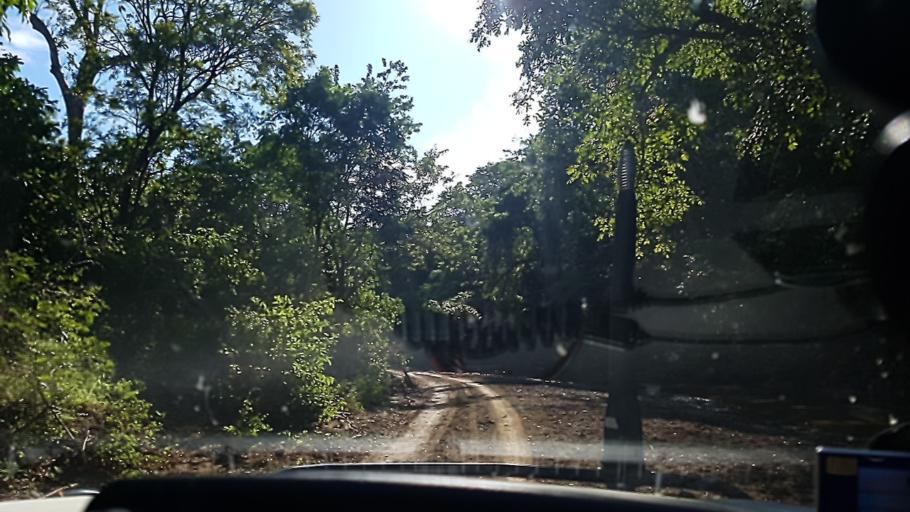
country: NI
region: Rivas
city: Tola
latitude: 11.5413
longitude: -86.1215
